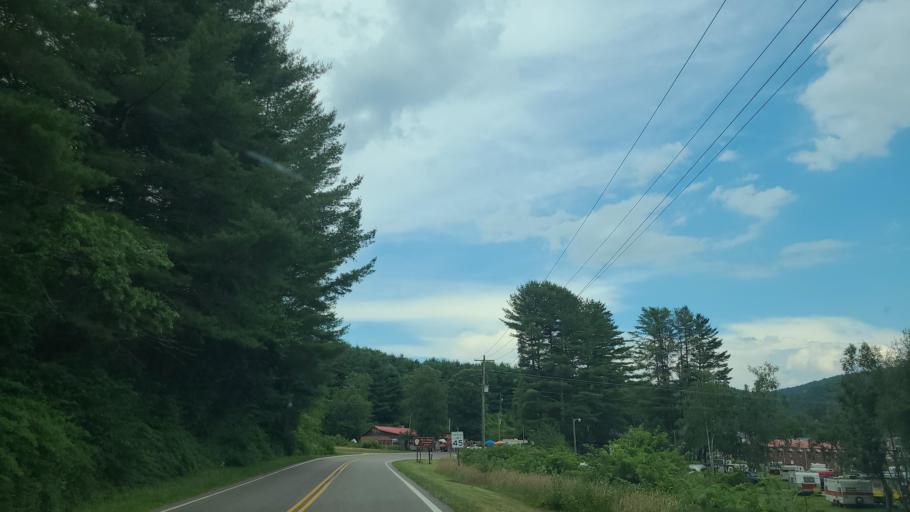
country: US
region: North Carolina
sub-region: Alleghany County
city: Sparta
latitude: 36.3946
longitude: -81.2487
